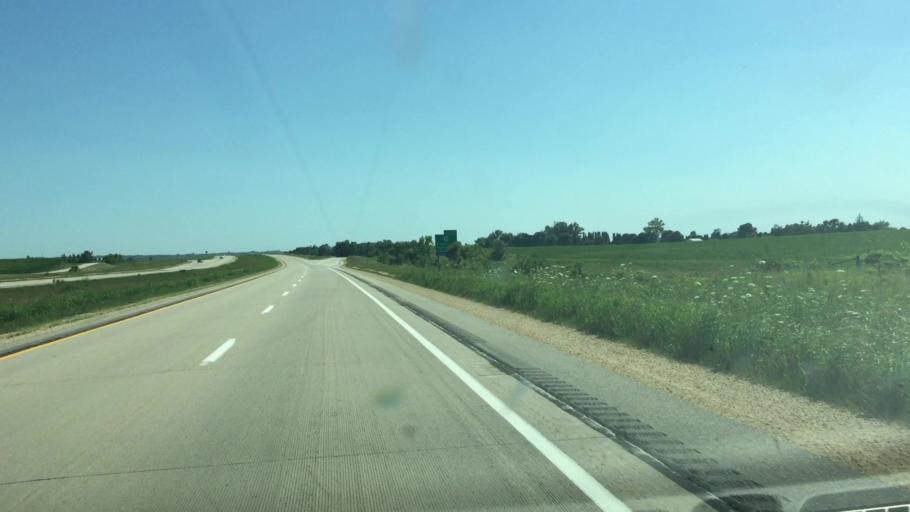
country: US
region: Iowa
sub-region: Jones County
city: Monticello
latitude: 42.2384
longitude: -91.1689
